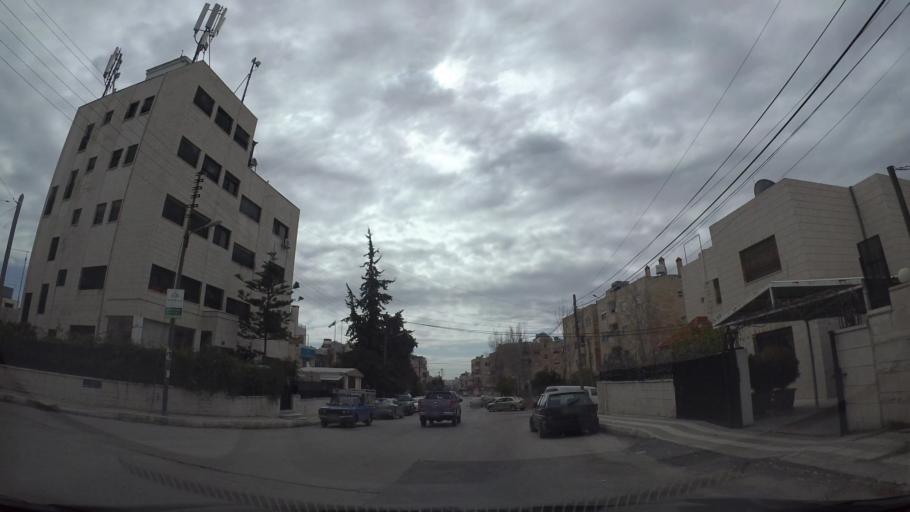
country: JO
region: Amman
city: Wadi as Sir
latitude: 31.9498
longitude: 35.8383
